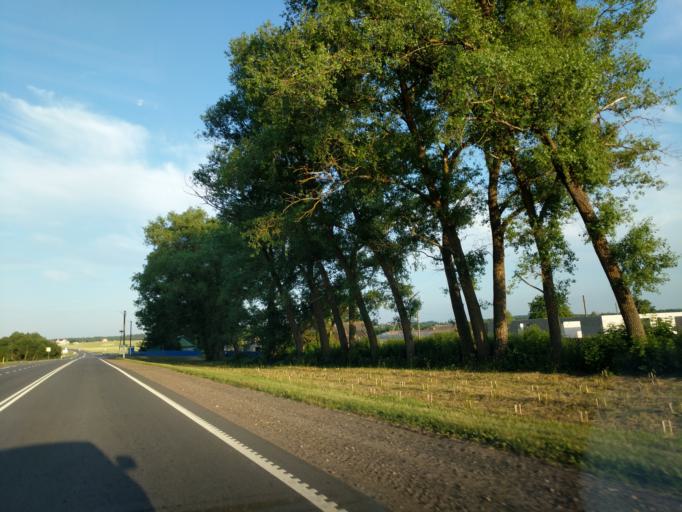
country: BY
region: Minsk
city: Syomkava
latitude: 54.1022
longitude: 27.4782
